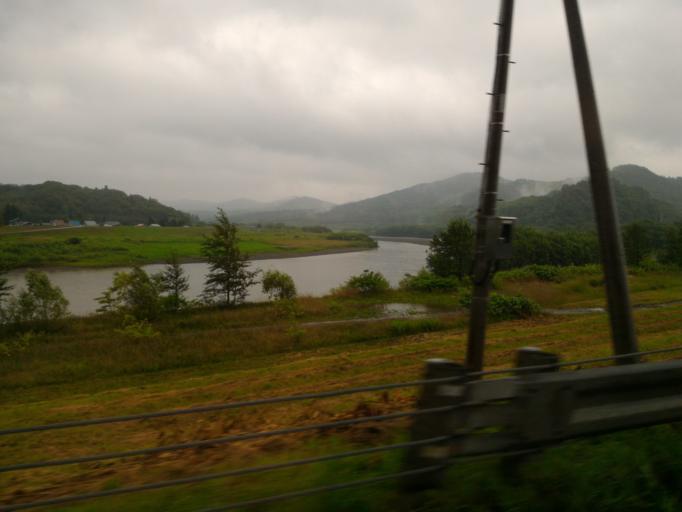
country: JP
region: Hokkaido
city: Nayoro
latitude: 44.7427
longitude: 142.0424
